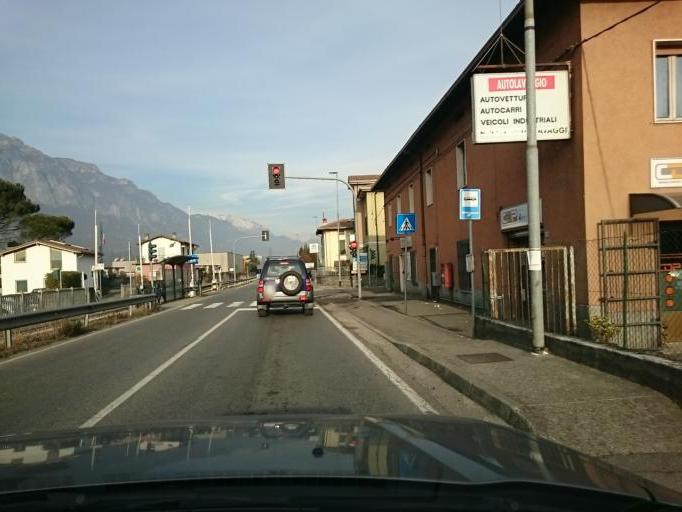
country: IT
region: Lombardy
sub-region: Provincia di Brescia
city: Artogne
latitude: 45.8580
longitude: 10.1584
